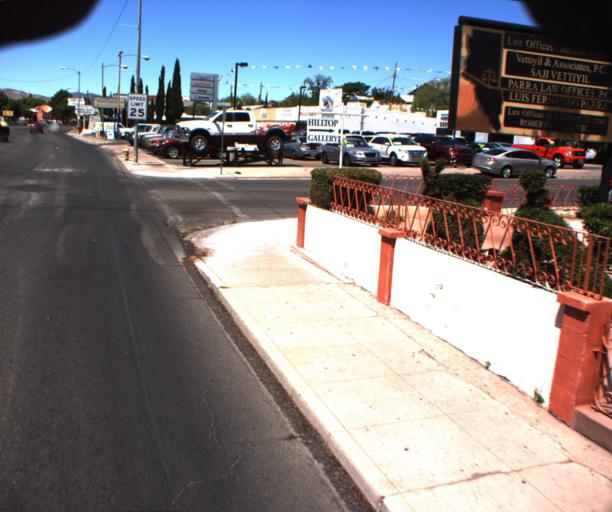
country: US
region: Arizona
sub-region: Santa Cruz County
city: Nogales
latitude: 31.3421
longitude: -110.9339
